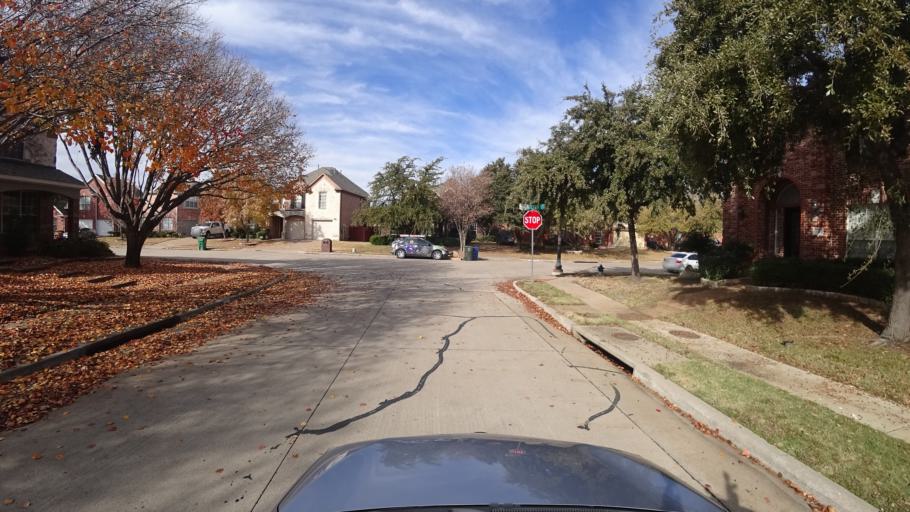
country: US
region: Texas
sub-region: Denton County
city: Lewisville
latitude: 33.0264
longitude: -96.9368
